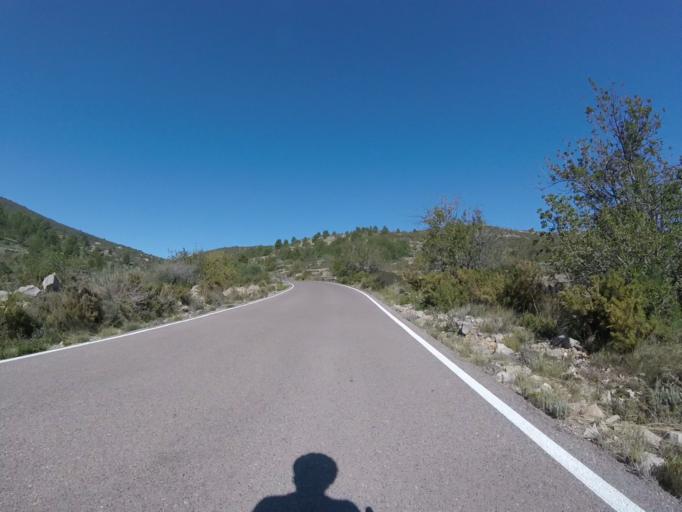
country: ES
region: Valencia
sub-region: Provincia de Castello
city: Santa Magdalena de Pulpis
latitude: 40.3832
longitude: 0.2616
